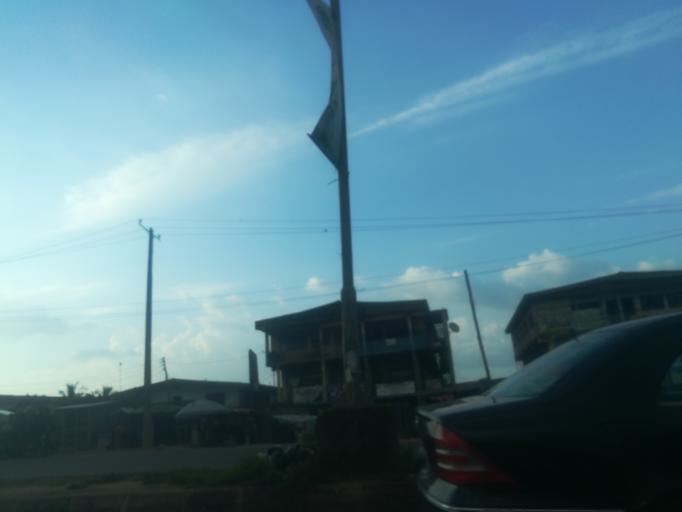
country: NG
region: Oyo
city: Ibadan
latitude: 7.4091
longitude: 3.9480
